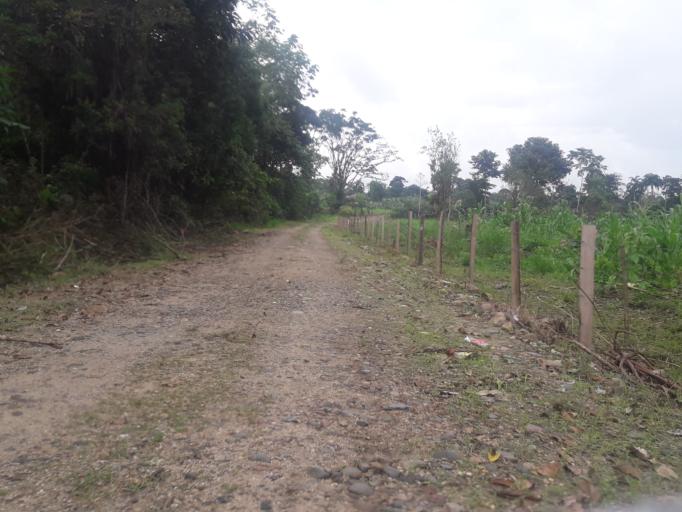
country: EC
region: Napo
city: Tena
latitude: -0.9788
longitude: -77.8457
